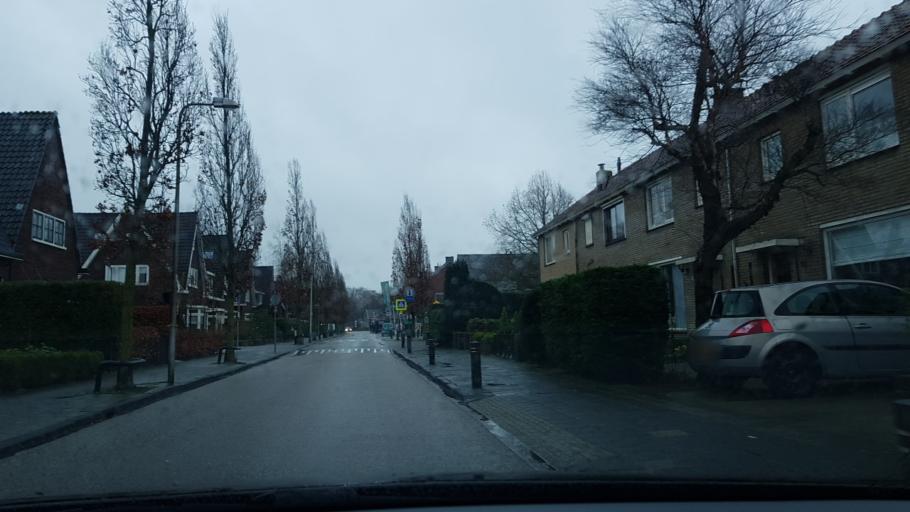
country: NL
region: North Holland
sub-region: Gemeente Bloemendaal
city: Bennebroek
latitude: 52.3259
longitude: 4.5913
